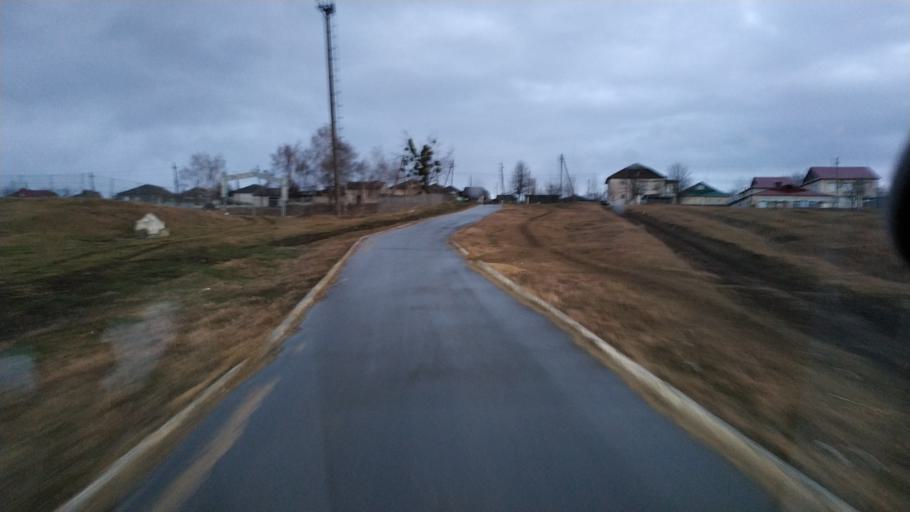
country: MD
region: Taraclia
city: Telenesti
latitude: 47.3734
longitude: 28.3774
